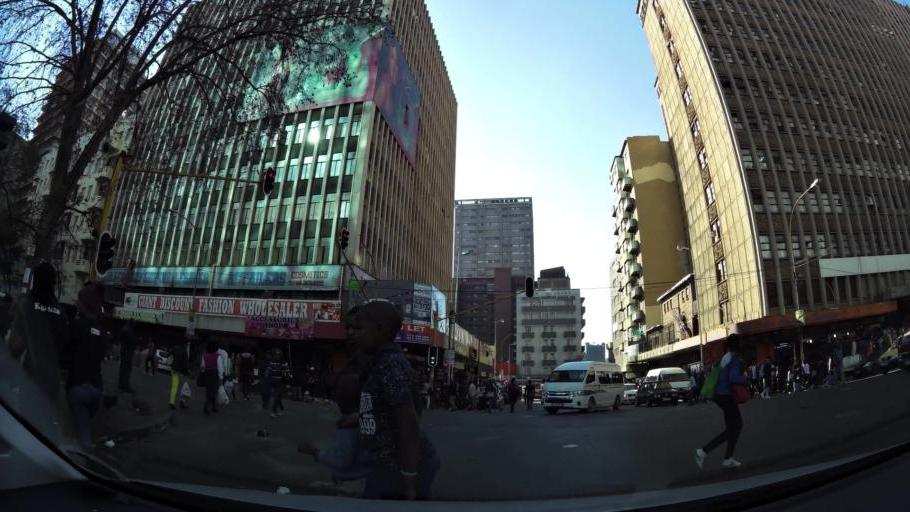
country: ZA
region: Gauteng
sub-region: City of Johannesburg Metropolitan Municipality
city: Johannesburg
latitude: -26.2011
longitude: 28.0469
